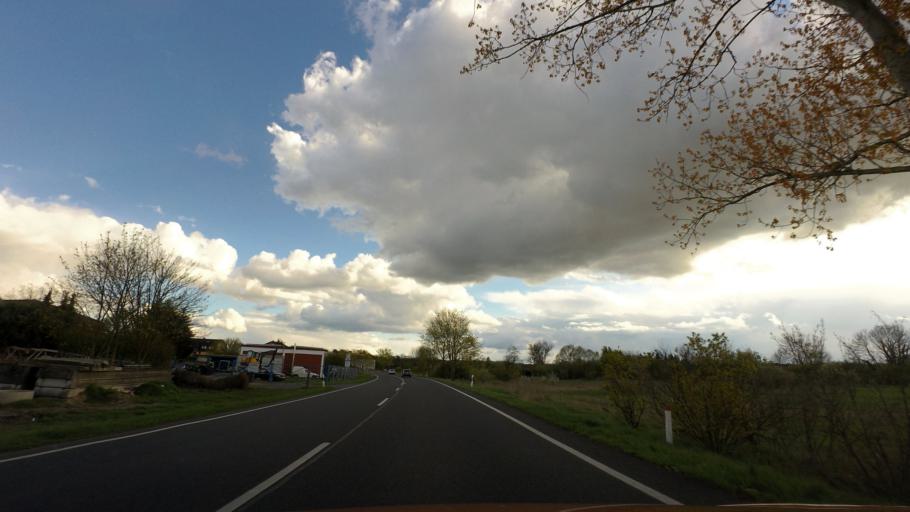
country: DE
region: Brandenburg
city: Friesack
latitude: 52.7411
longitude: 12.5727
